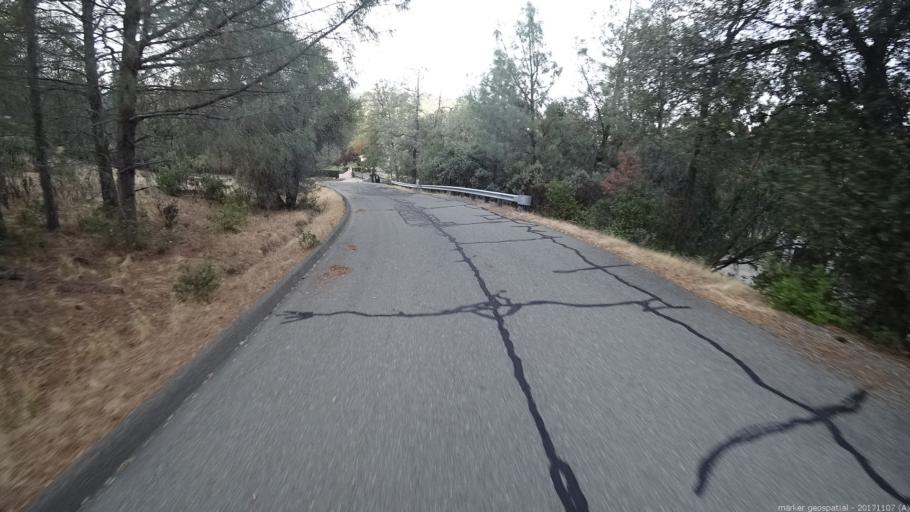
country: US
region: California
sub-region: Shasta County
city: Shasta
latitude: 40.5390
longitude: -122.4876
